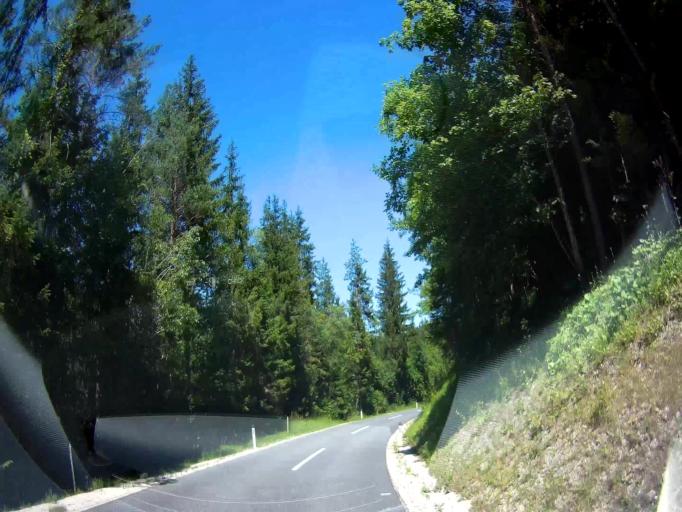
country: AT
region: Carinthia
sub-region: Politischer Bezirk Klagenfurt Land
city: Ferlach
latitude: 46.5111
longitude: 14.2917
